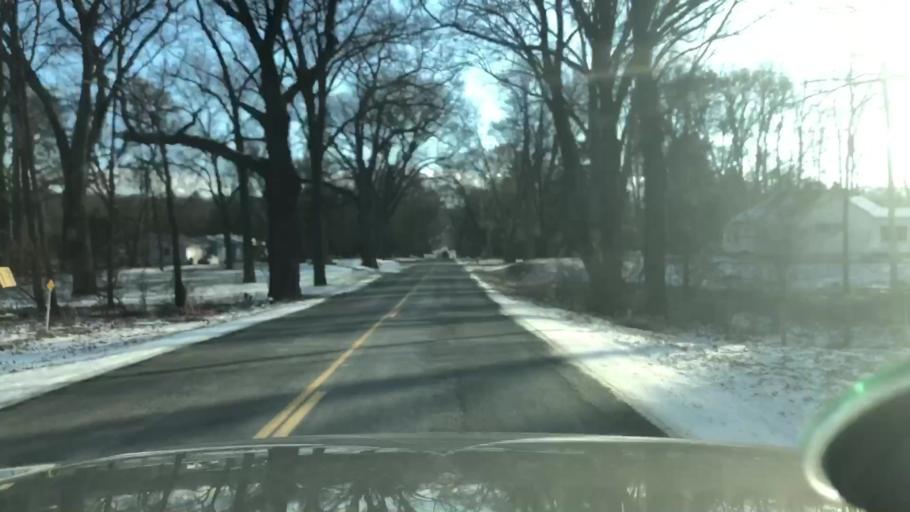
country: US
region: Michigan
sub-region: Jackson County
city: Vandercook Lake
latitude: 42.1528
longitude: -84.4520
